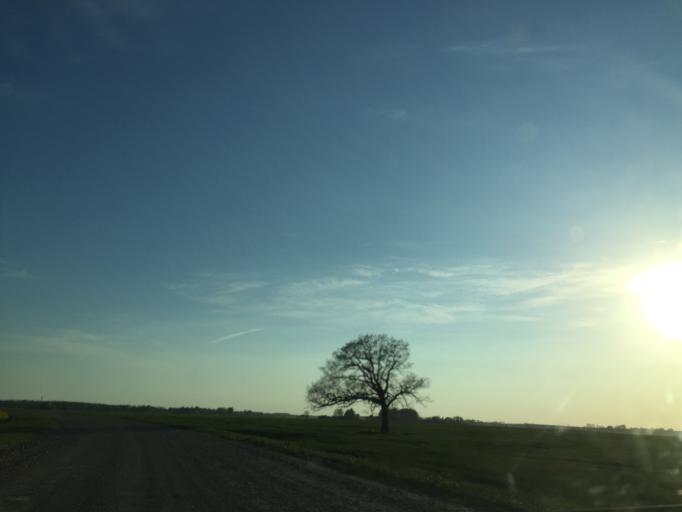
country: LV
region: Bauskas Rajons
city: Bauska
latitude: 56.2840
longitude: 24.2208
